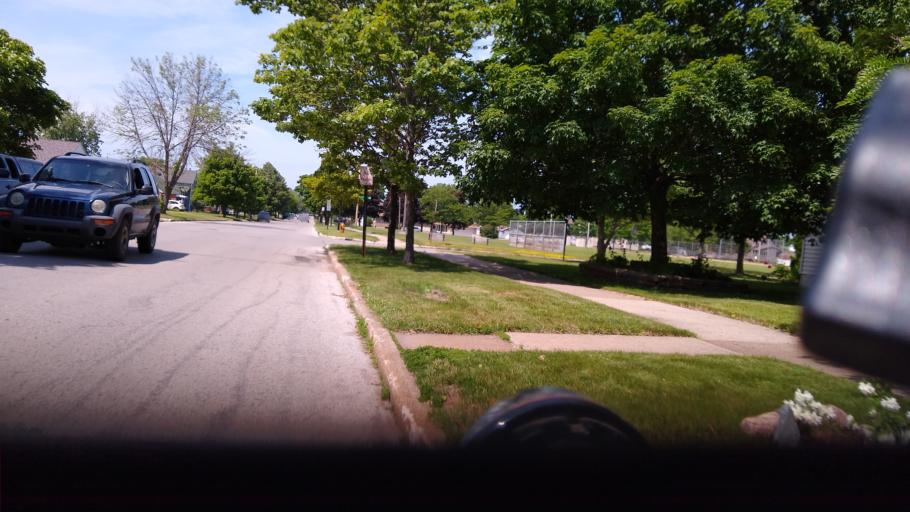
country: US
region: Michigan
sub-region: Delta County
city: Escanaba
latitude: 45.7369
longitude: -87.0739
